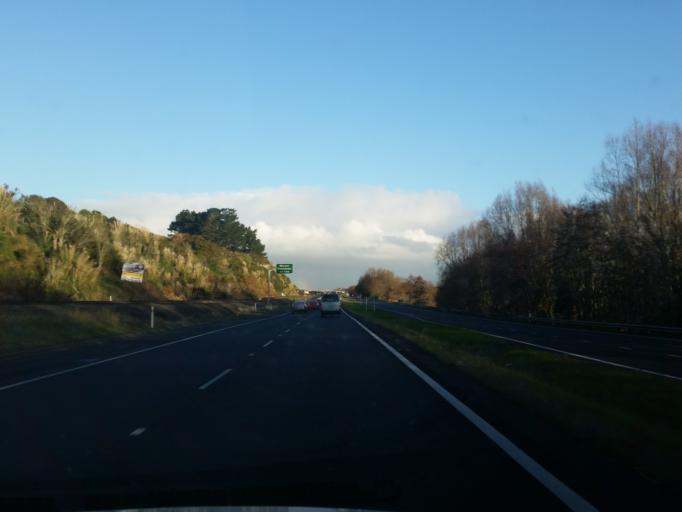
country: NZ
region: Auckland
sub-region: Auckland
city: Pukekohe East
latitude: -37.2656
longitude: 175.0449
